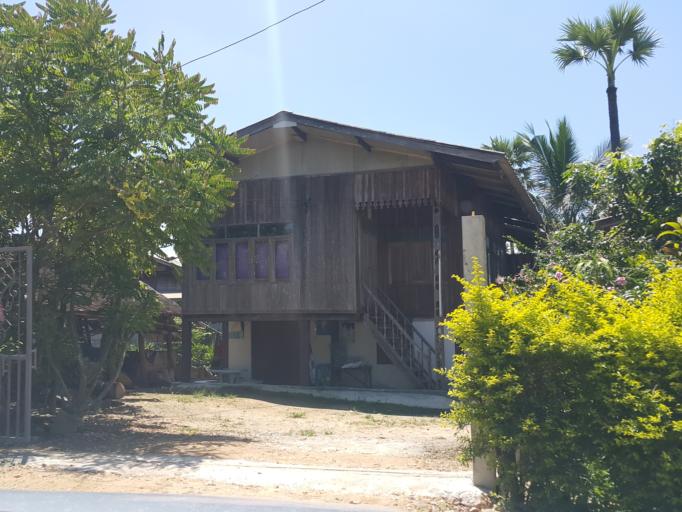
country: TH
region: Lamphun
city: Ban Thi
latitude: 18.6668
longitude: 99.1543
